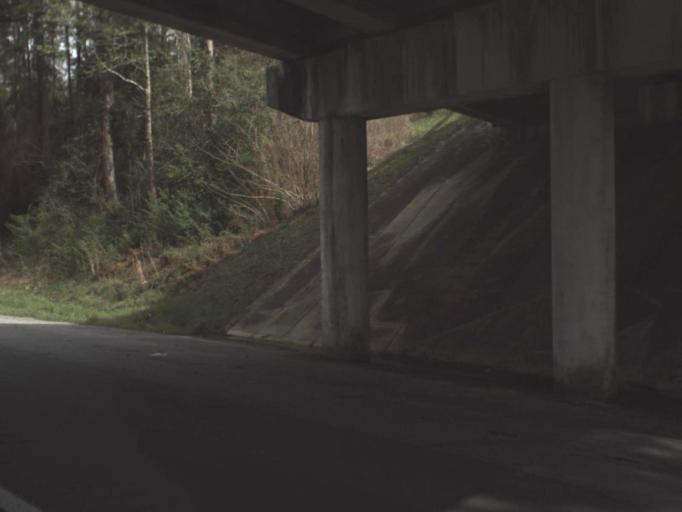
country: US
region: Florida
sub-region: Walton County
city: DeFuniak Springs
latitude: 30.6910
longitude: -86.0729
